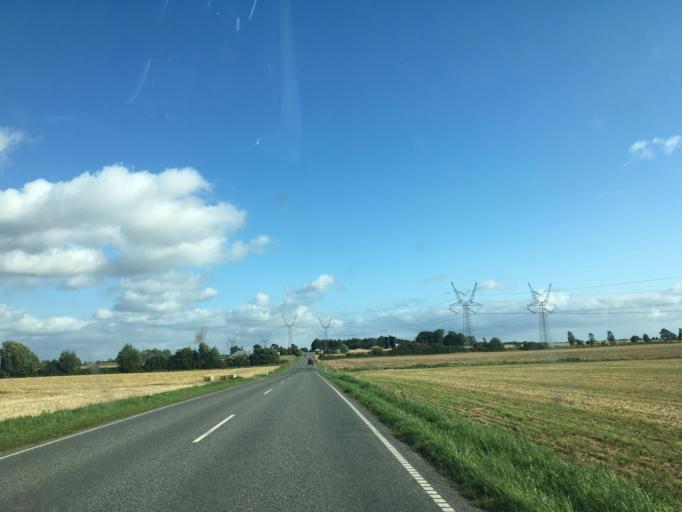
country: DK
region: South Denmark
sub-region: Middelfart Kommune
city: Norre Aby
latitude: 55.4679
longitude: 9.8126
